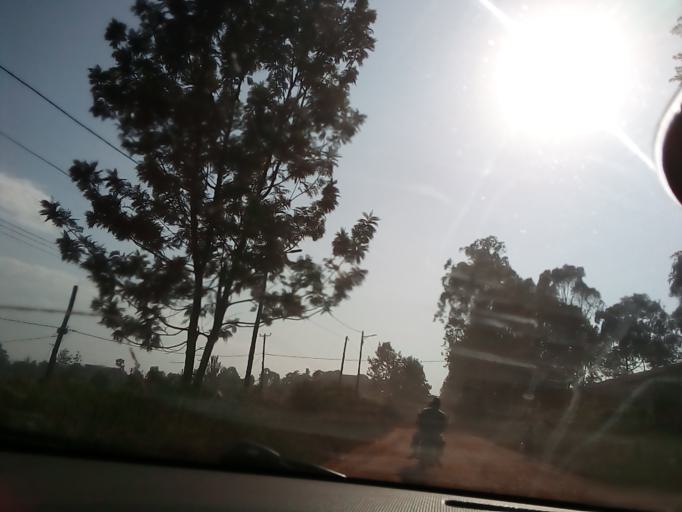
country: UG
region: Central Region
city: Masaka
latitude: -0.3356
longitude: 31.7322
